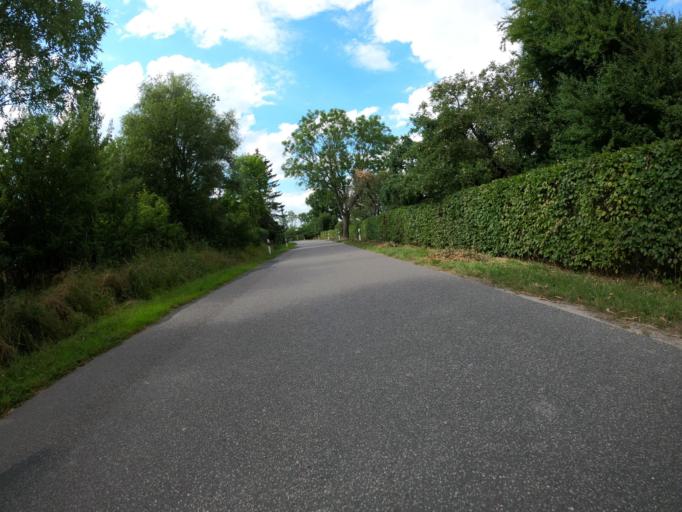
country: DE
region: Mecklenburg-Vorpommern
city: Woldegk
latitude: 53.4361
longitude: 13.5991
